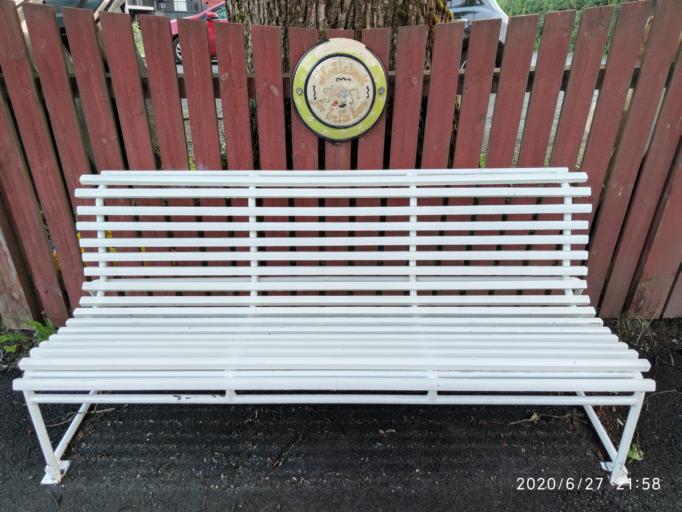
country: NO
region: Buskerud
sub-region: Kongsberg
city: Kongsberg
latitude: 59.6636
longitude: 9.6503
